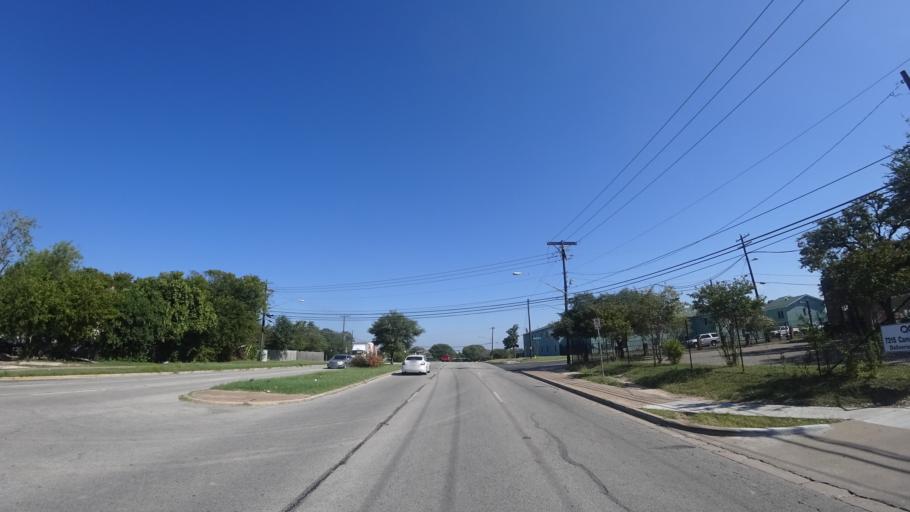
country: US
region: Texas
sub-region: Travis County
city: Austin
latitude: 30.3270
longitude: -97.6916
